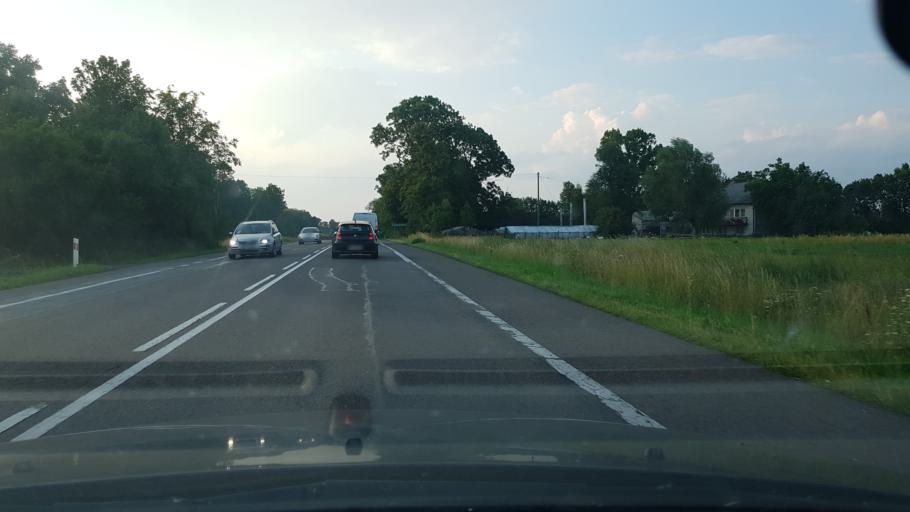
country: PL
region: Masovian Voivodeship
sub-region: Powiat ciechanowski
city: Glinojeck
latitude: 52.7428
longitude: 20.3175
